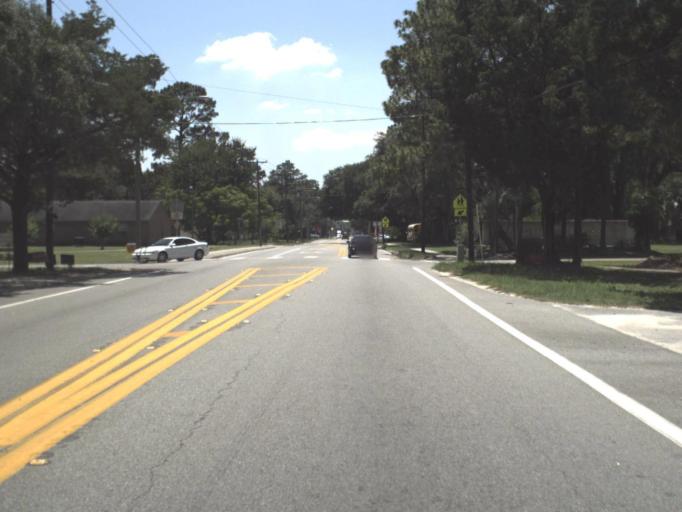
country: US
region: Florida
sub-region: Lafayette County
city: Mayo
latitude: 30.0531
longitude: -83.1673
